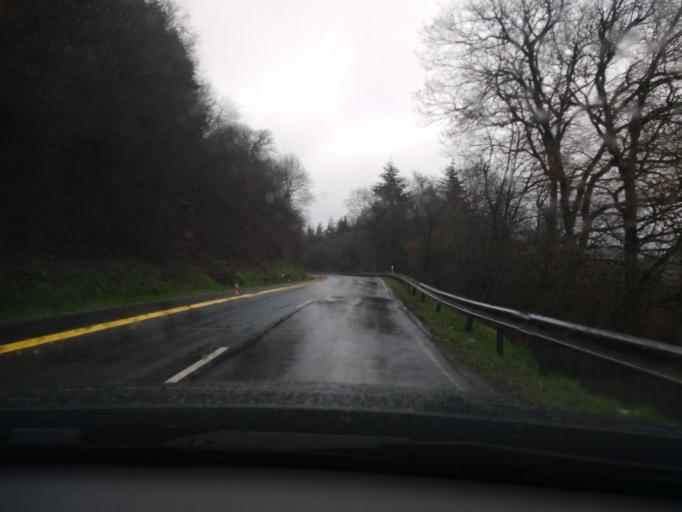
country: DE
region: Rheinland-Pfalz
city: Pluwig
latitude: 49.6836
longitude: 6.7266
